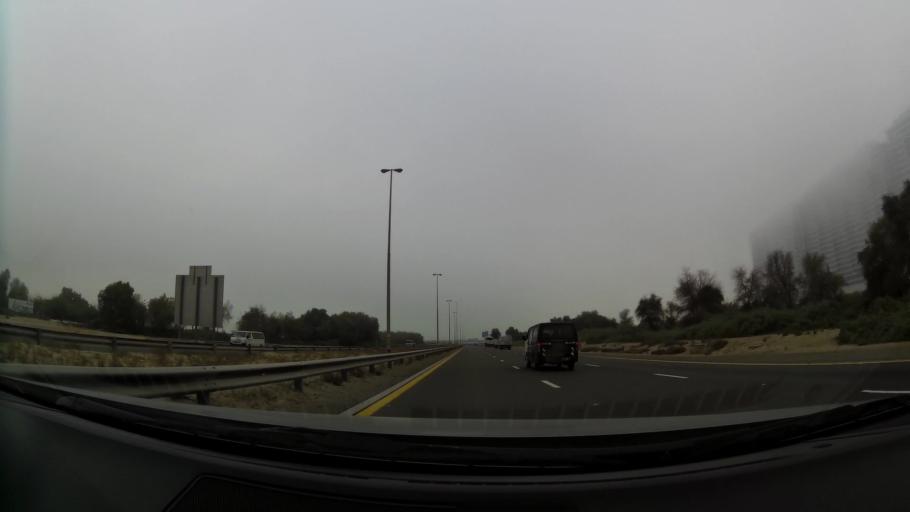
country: AE
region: Dubai
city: Dubai
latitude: 25.0934
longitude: 55.3871
